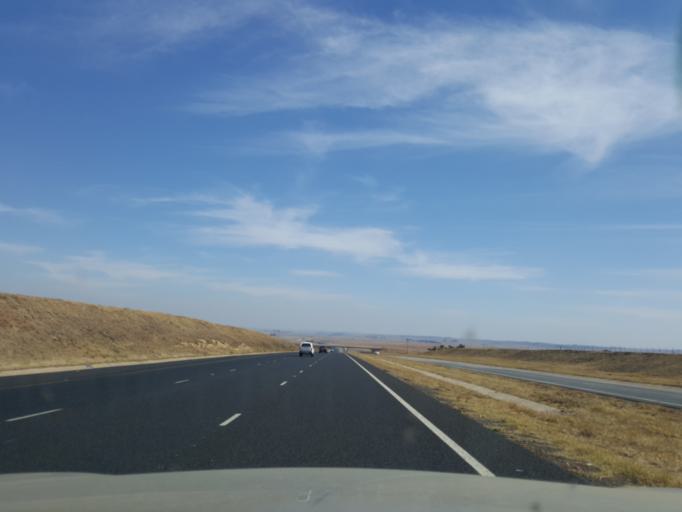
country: ZA
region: Mpumalanga
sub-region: Nkangala District Municipality
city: Belfast
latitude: -25.8222
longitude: 29.8565
